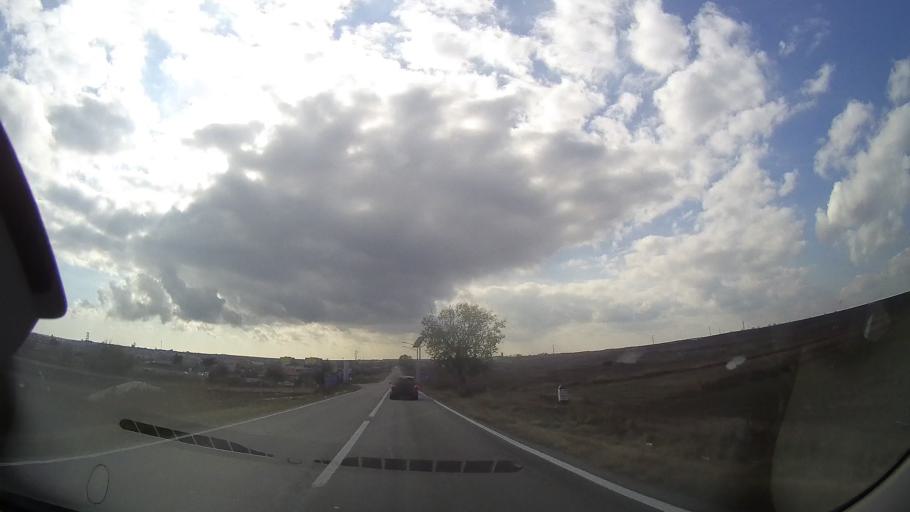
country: RO
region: Constanta
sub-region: Oras Techirghiol
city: Techirghiol
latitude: 44.0666
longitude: 28.5940
